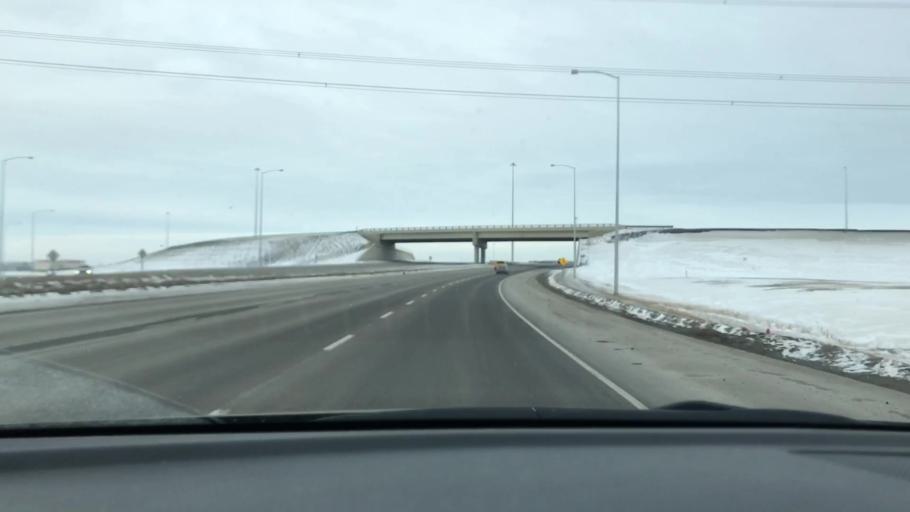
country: CA
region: Alberta
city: Sherwood Park
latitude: 53.5123
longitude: -113.3372
